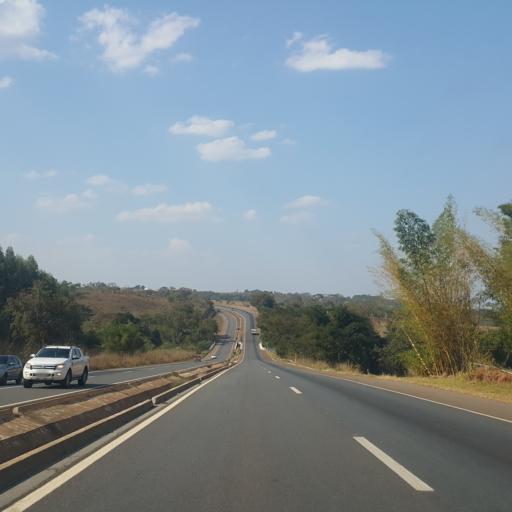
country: BR
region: Goias
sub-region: Abadiania
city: Abadiania
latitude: -16.2986
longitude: -48.8077
